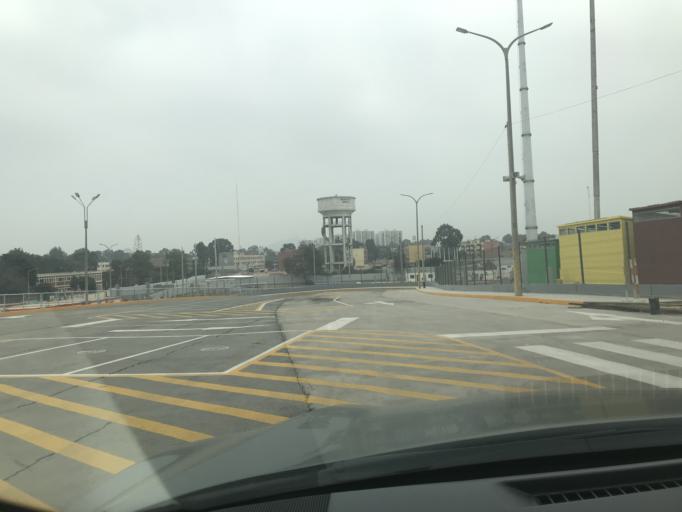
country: PE
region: Callao
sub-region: Callao
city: Callao
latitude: -12.0568
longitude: -77.0844
